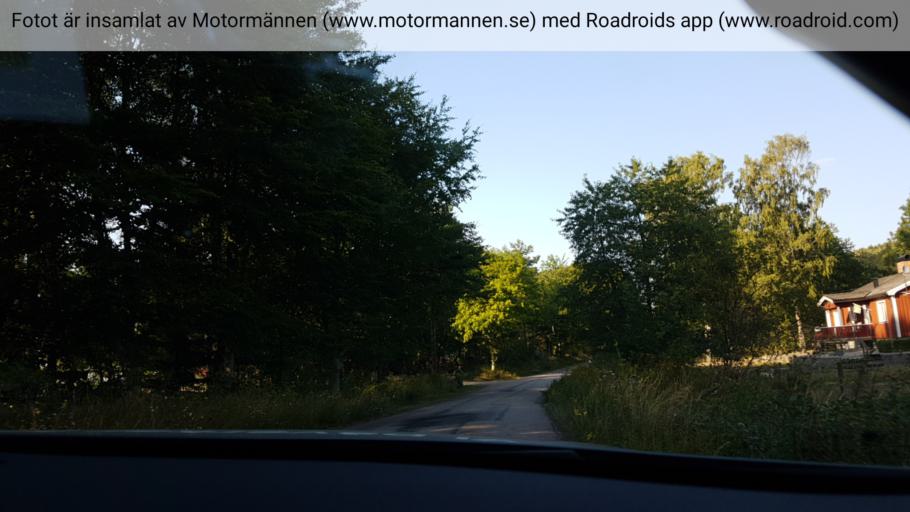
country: SE
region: Vaestra Goetaland
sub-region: Skara Kommun
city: Axvall
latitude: 58.4212
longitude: 13.6800
